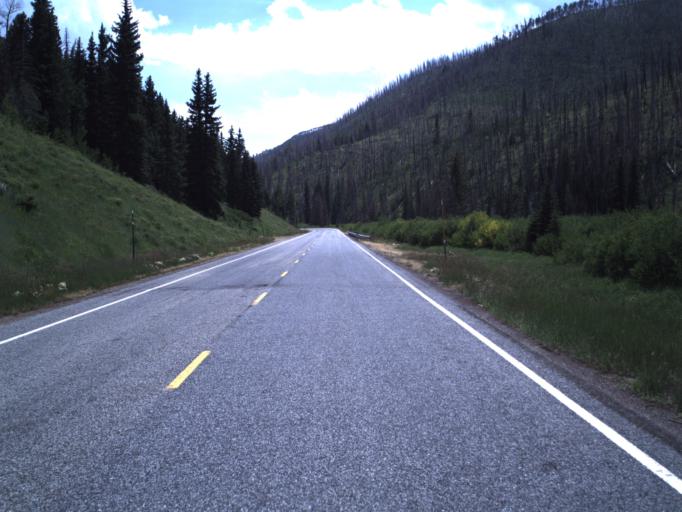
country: US
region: Utah
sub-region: Sanpete County
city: Fairview
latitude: 39.5588
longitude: -111.1745
